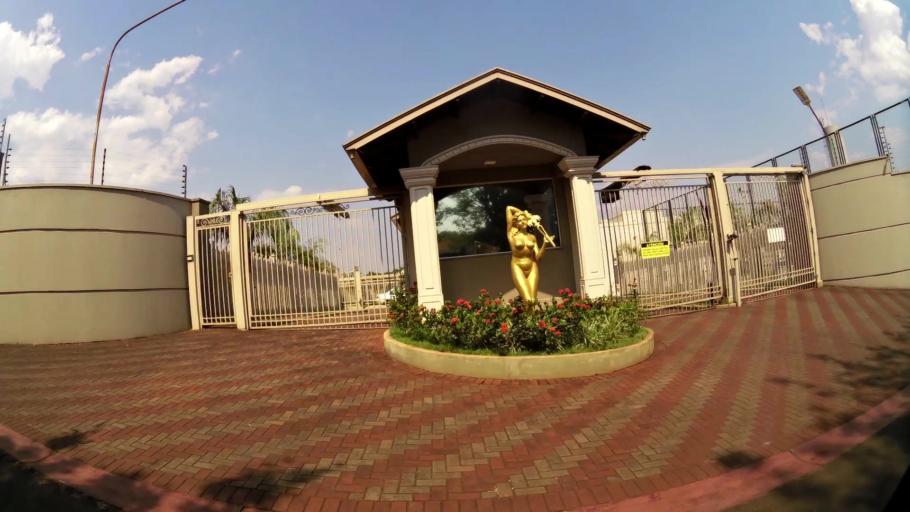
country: PY
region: Alto Parana
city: Ciudad del Este
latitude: -25.5141
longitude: -54.6252
